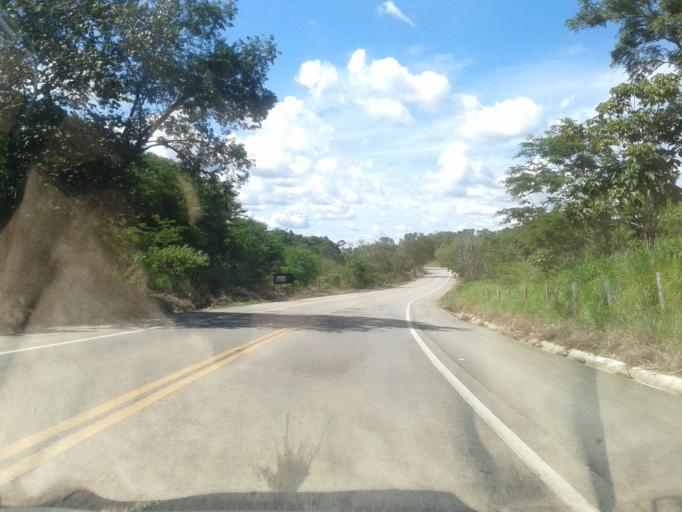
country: BR
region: Goias
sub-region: Goias
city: Goias
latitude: -15.6628
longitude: -50.2181
